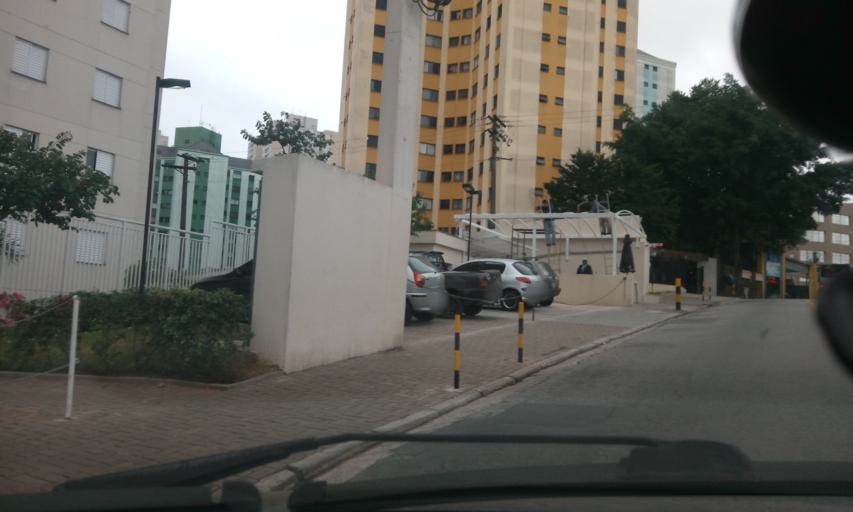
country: BR
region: Sao Paulo
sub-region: Taboao Da Serra
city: Taboao da Serra
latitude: -23.6187
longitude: -46.7718
